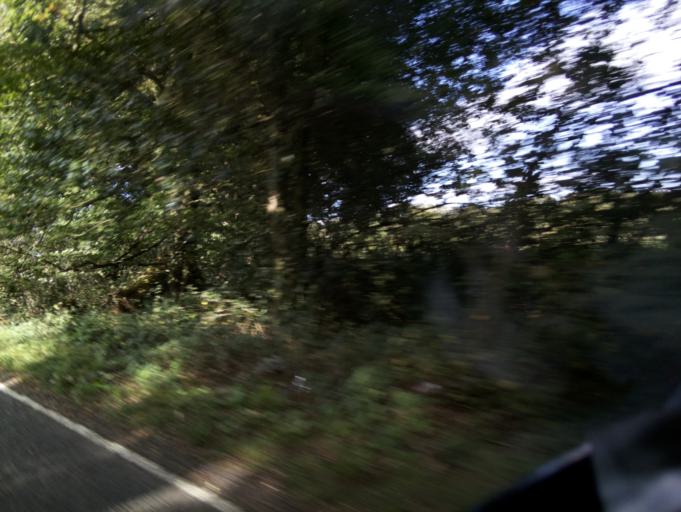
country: GB
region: England
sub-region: Hampshire
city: Basingstoke
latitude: 51.2177
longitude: -1.0602
